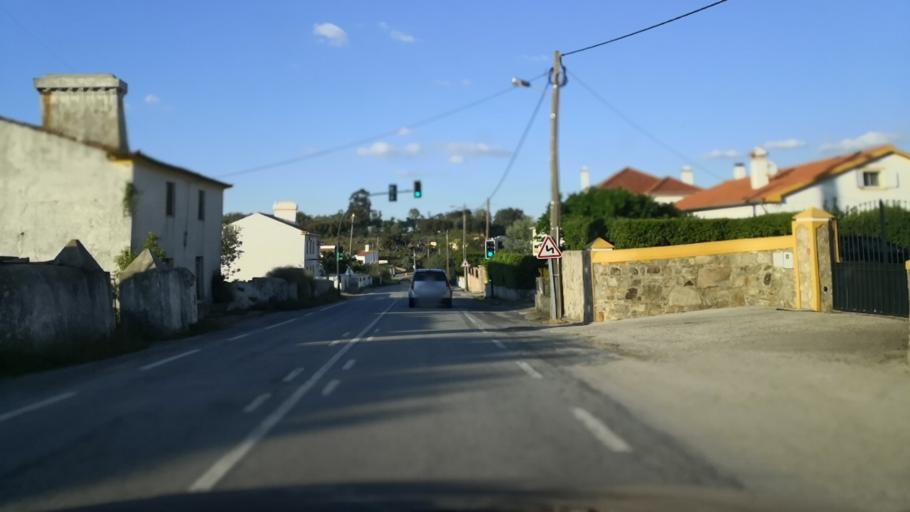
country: PT
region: Portalegre
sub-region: Marvao
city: Marvao
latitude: 39.3588
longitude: -7.4051
